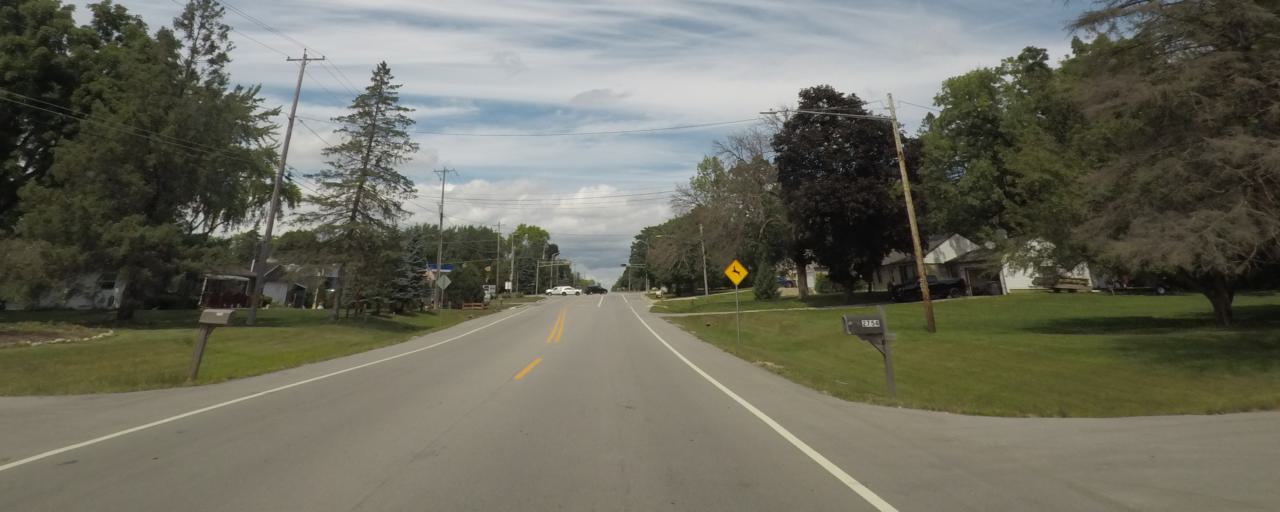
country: US
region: Wisconsin
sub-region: Waukesha County
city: New Berlin
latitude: 42.9942
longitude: -88.0680
